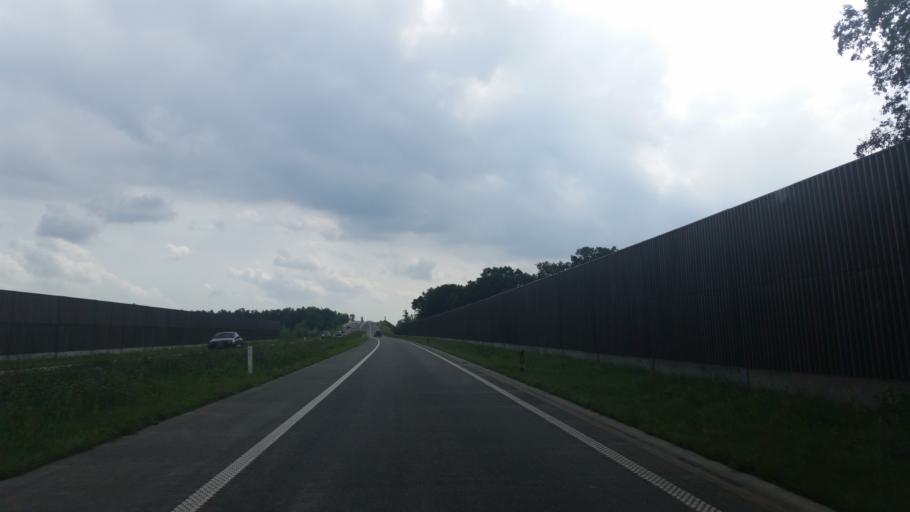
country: BE
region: Flanders
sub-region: Provincie Antwerpen
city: Kasterlee
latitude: 51.2049
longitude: 4.9687
